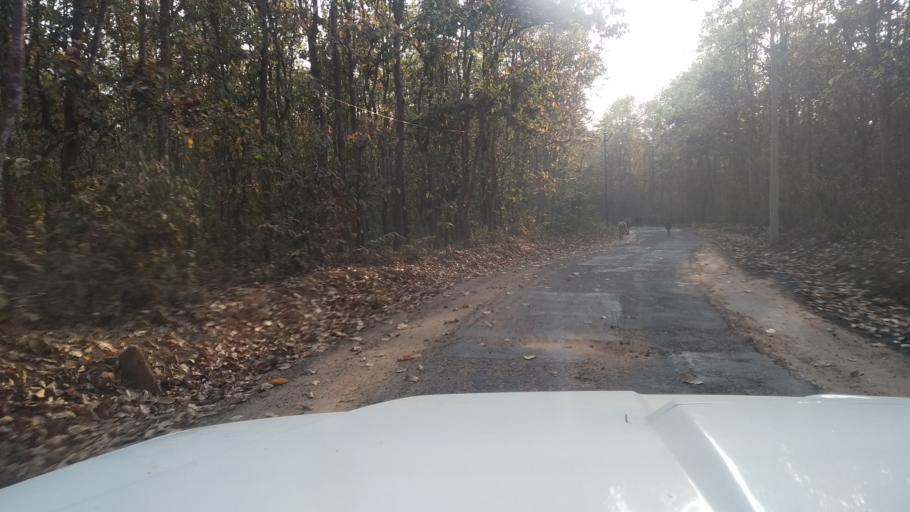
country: IN
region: Tripura
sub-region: West Tripura
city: Sonamura
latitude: 23.3335
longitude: 91.3126
